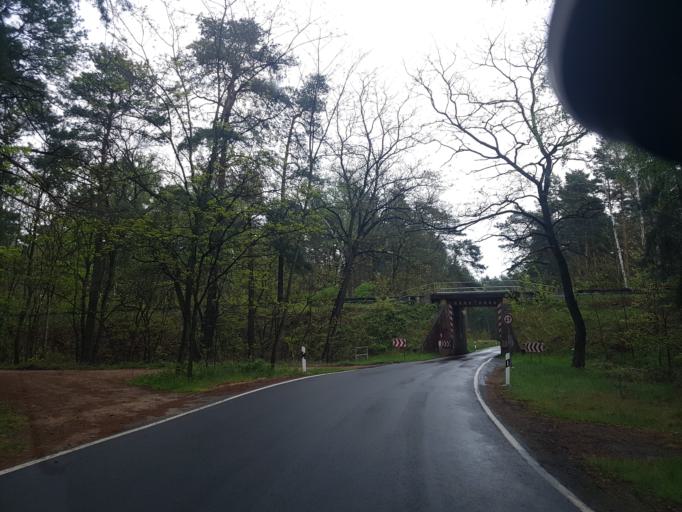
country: DE
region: Brandenburg
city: Spremberg
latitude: 51.6322
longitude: 14.4294
